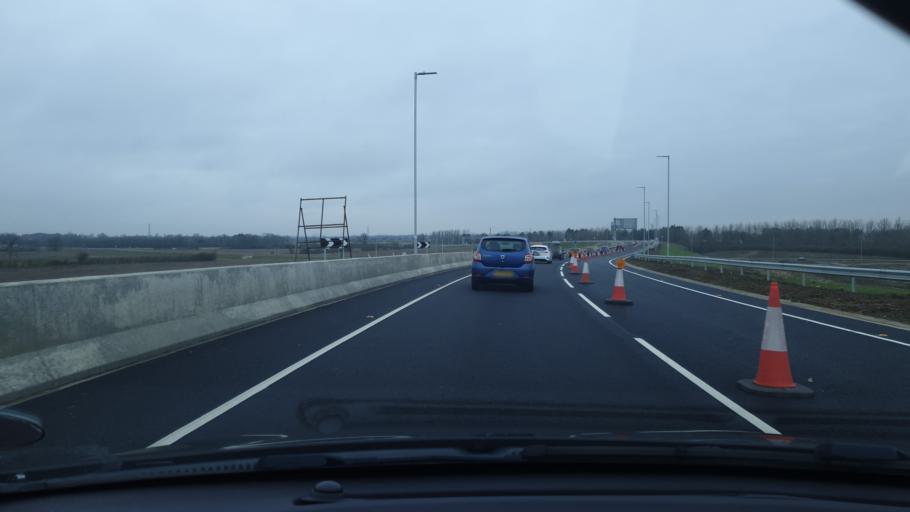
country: GB
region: England
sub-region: Cambridgeshire
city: Girton
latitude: 52.2321
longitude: 0.0623
